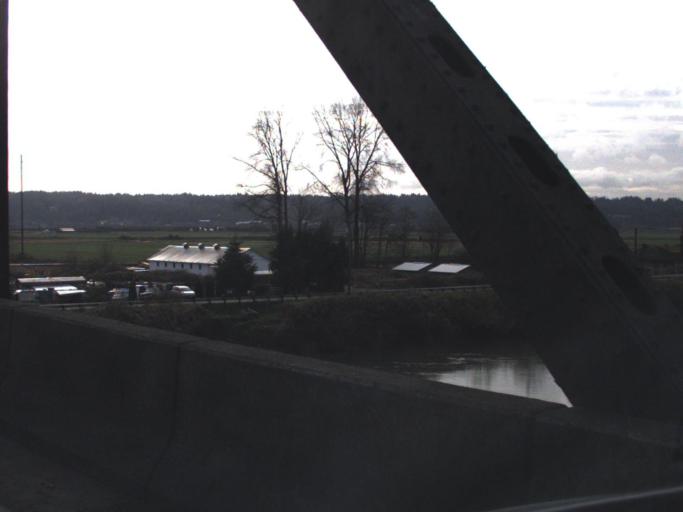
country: US
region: Washington
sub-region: Snohomish County
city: Snohomish
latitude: 47.9123
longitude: -122.1087
